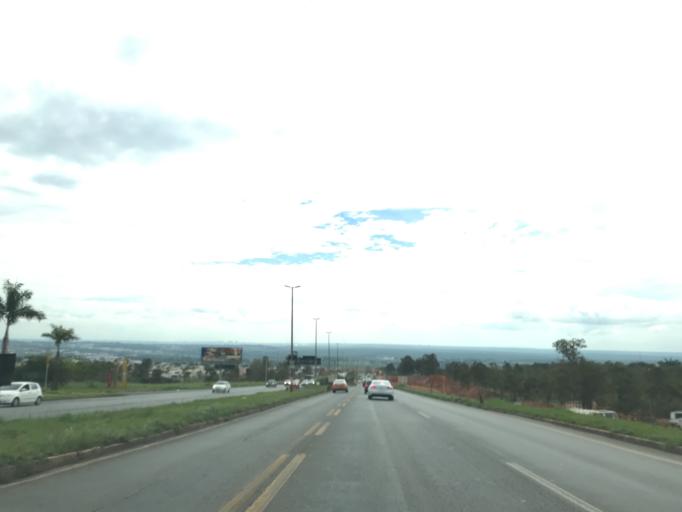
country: BR
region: Federal District
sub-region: Brasilia
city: Brasilia
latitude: -15.6906
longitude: -47.8641
